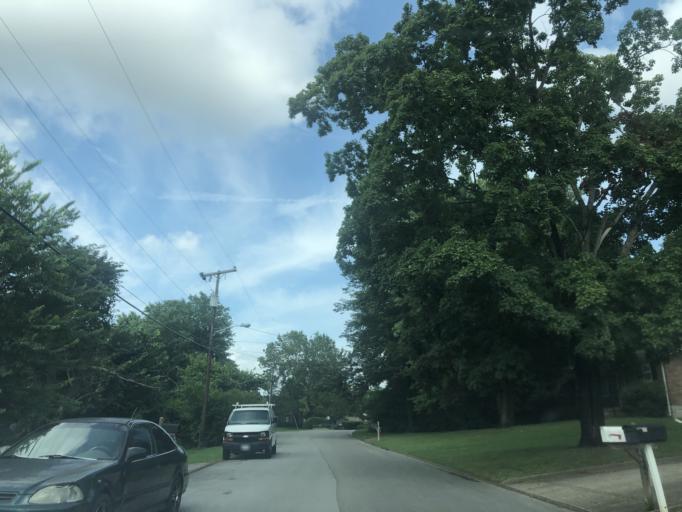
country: US
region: Tennessee
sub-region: Davidson County
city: Lakewood
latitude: 36.1583
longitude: -86.6284
